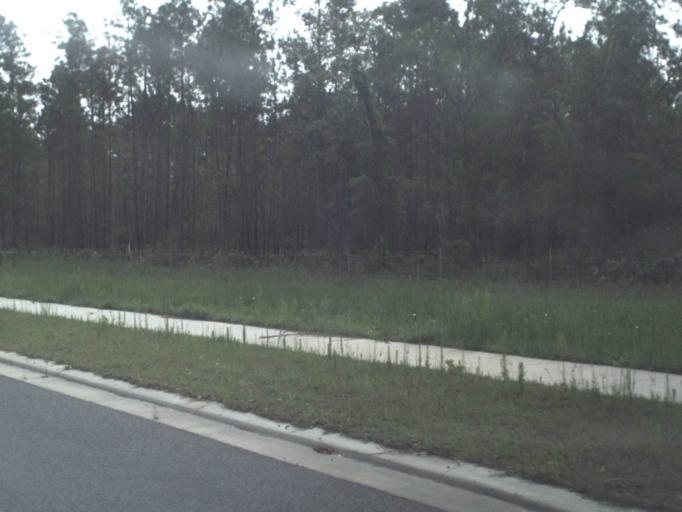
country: US
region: Florida
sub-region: Duval County
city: Baldwin
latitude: 30.3939
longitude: -81.9352
